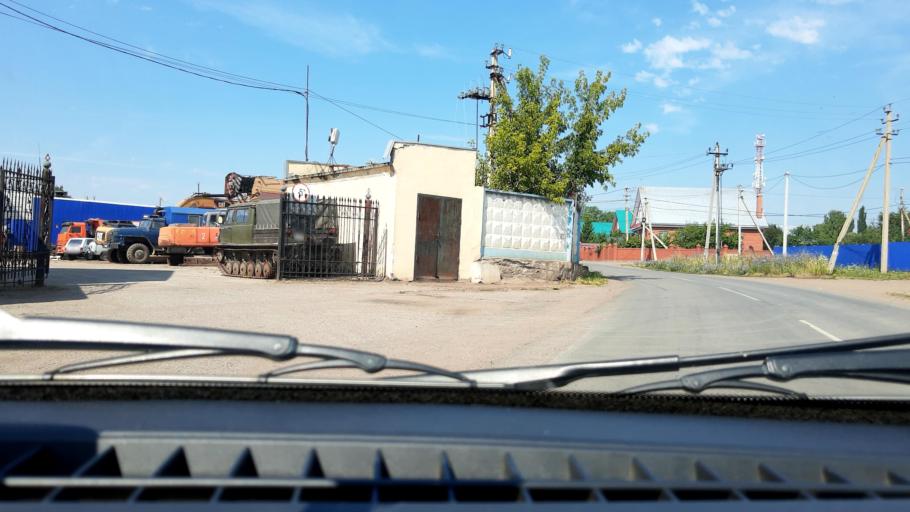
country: RU
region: Bashkortostan
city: Mikhaylovka
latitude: 54.8055
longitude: 55.7975
